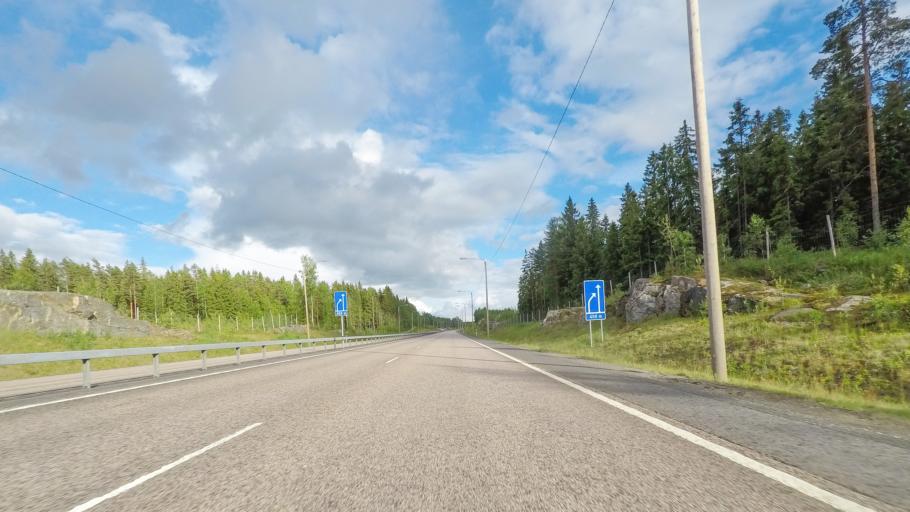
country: FI
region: Paijanne Tavastia
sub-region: Lahti
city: Hartola
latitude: 61.4205
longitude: 26.0270
